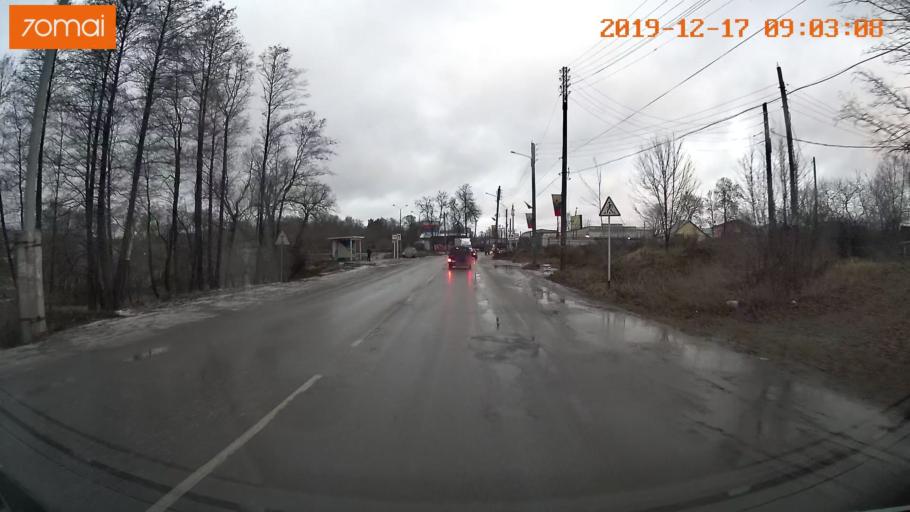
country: RU
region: Vladimir
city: Kosterevo
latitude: 55.9556
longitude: 39.6328
